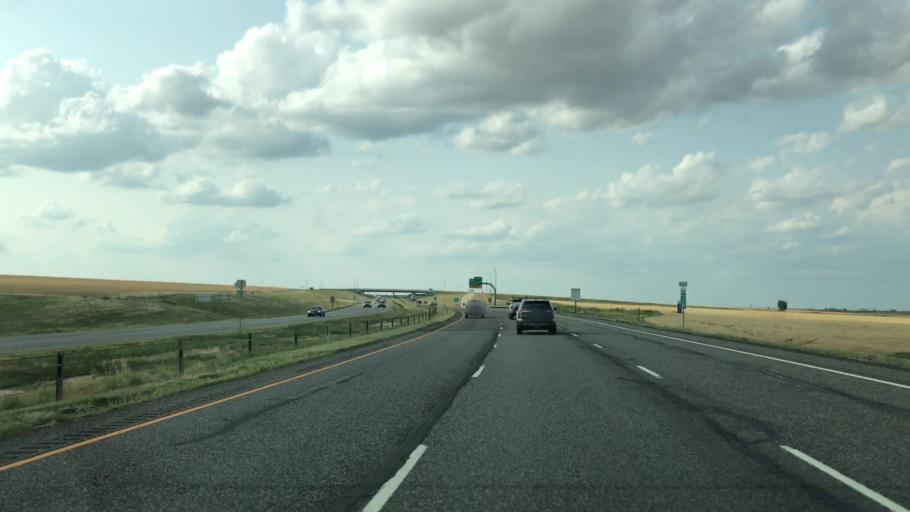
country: US
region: Colorado
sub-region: Adams County
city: Aurora
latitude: 39.8054
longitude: -104.7166
